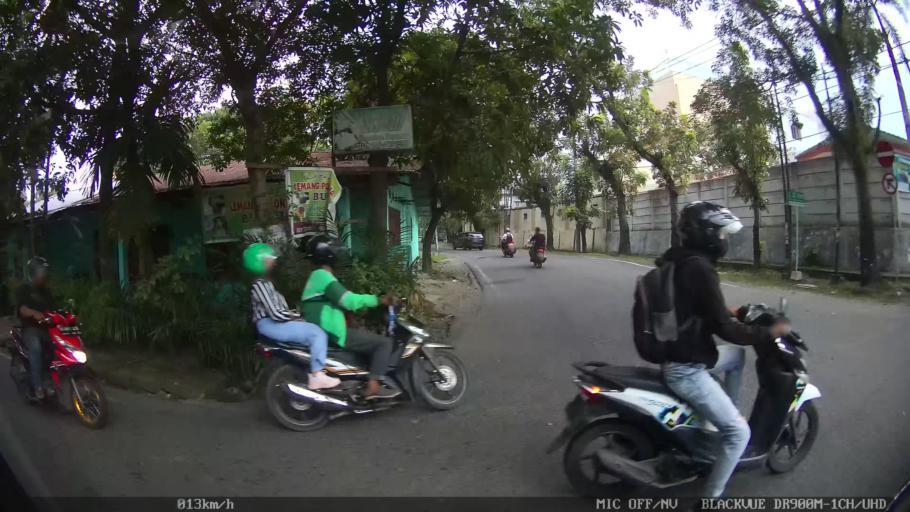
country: ID
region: North Sumatra
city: Medan
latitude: 3.5566
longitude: 98.6820
